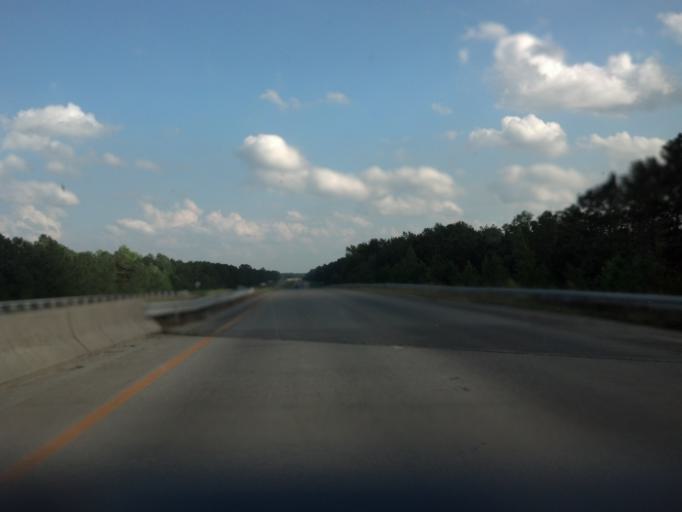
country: US
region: North Carolina
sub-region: Edgecombe County
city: Tarboro
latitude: 35.9173
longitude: -77.6562
